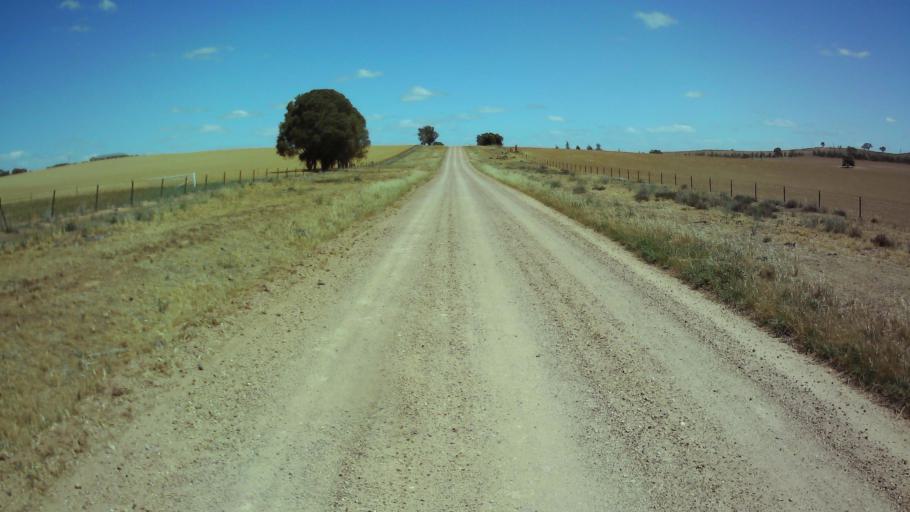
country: AU
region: New South Wales
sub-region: Weddin
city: Grenfell
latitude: -33.9464
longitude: 148.3292
